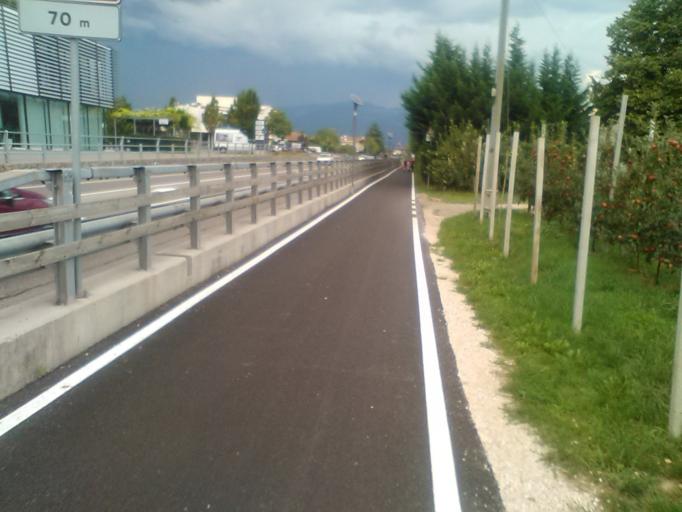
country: IT
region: Trentino-Alto Adige
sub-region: Bolzano
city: San Michele
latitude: 46.4478
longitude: 11.2647
